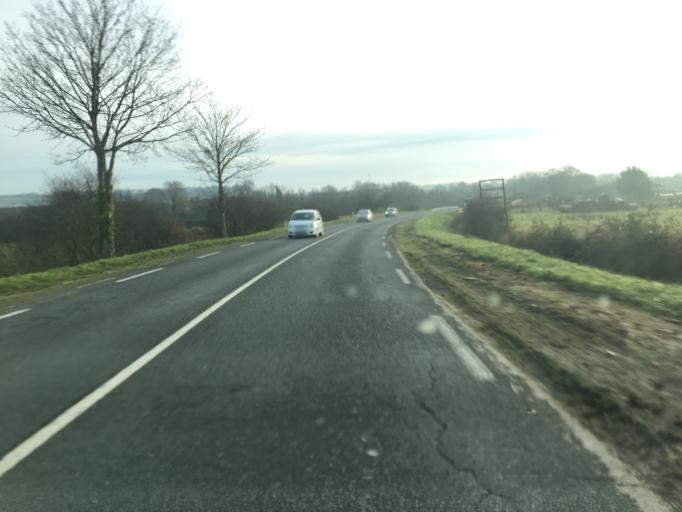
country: FR
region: Lower Normandy
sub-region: Departement du Calvados
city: Dives-sur-Mer
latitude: 49.2740
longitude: -0.1072
